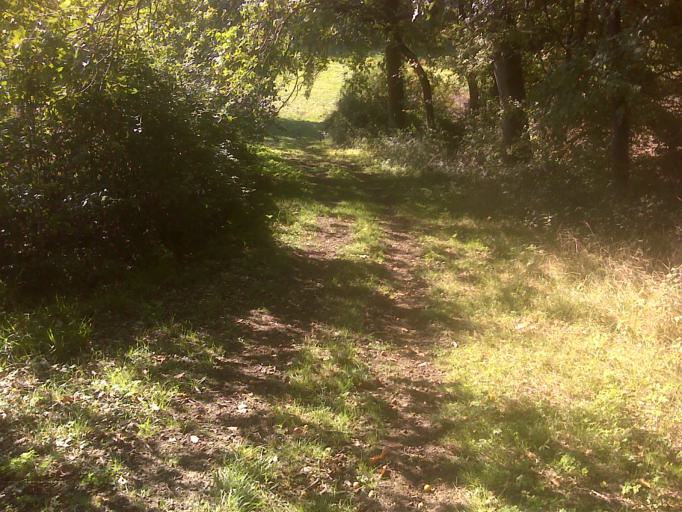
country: FR
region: Midi-Pyrenees
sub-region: Departement du Gers
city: Lectoure
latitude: 43.9524
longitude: 0.6334
